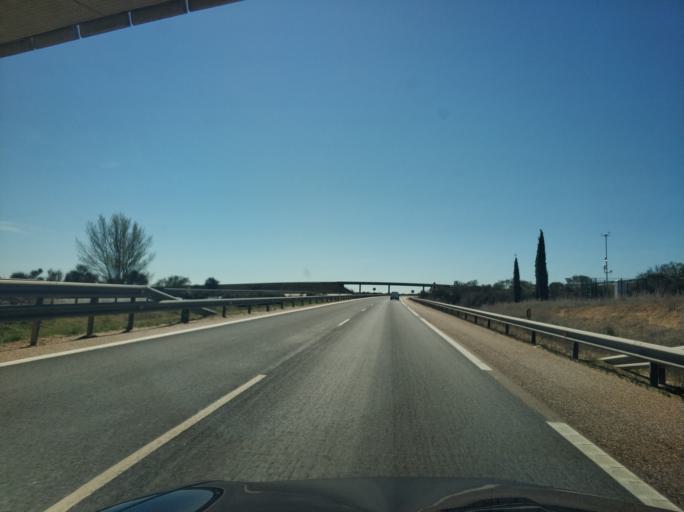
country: ES
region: Castille and Leon
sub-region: Provincia de Zamora
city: Canizal
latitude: 41.1740
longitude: -5.3742
